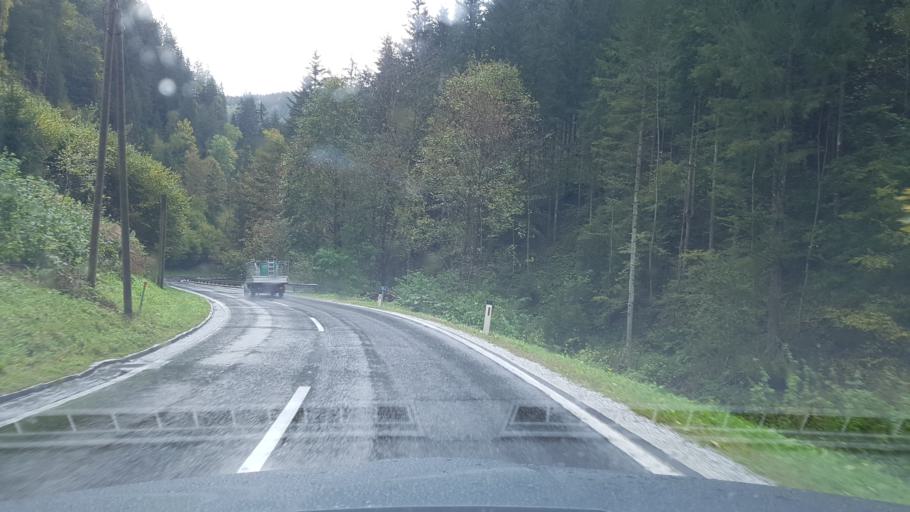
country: AT
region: Styria
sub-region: Politischer Bezirk Voitsberg
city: Salla
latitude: 47.1125
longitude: 14.9991
